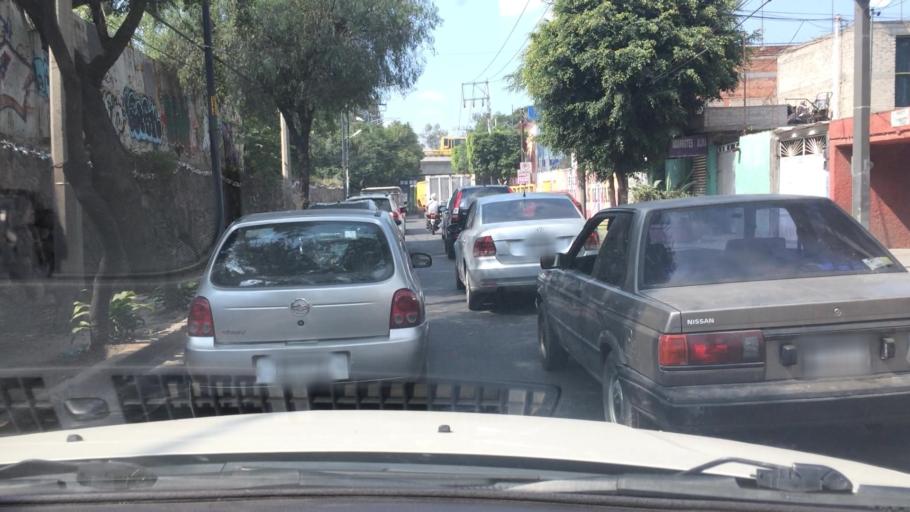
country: MX
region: Mexico
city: Colonia Lindavista
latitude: 19.5192
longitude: -99.1334
